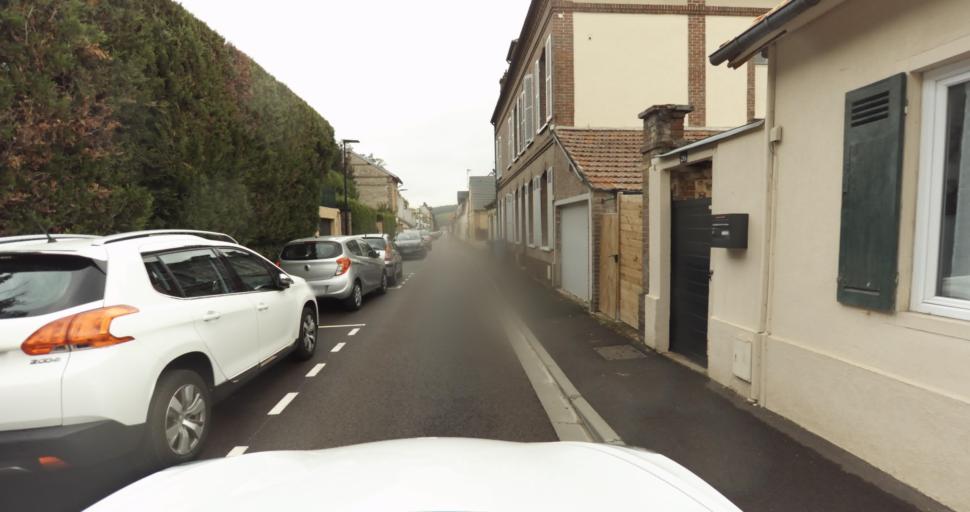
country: FR
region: Haute-Normandie
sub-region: Departement de l'Eure
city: Evreux
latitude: 49.0314
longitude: 1.1501
